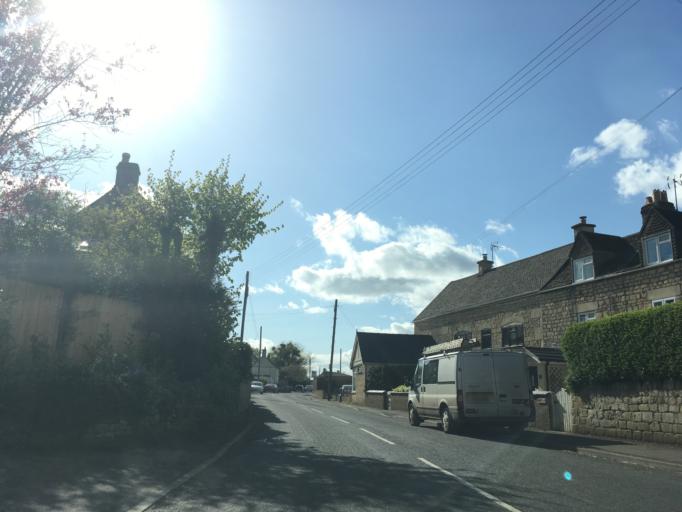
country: GB
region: England
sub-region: Gloucestershire
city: Stonehouse
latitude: 51.7269
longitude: -2.2623
